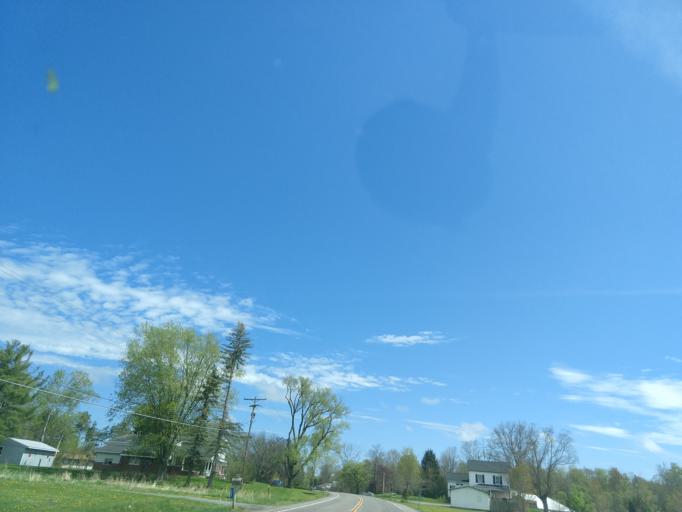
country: US
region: New York
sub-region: Tompkins County
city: Dryden
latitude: 42.5025
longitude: -76.3616
